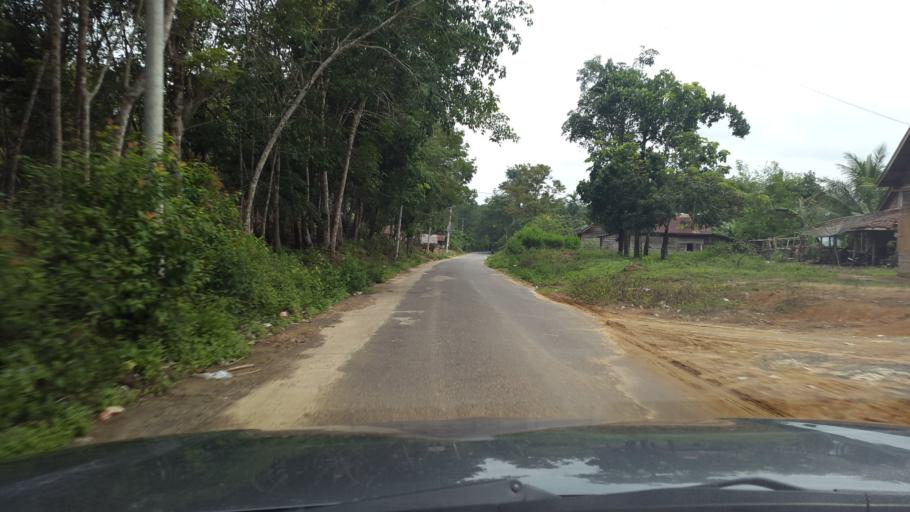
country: ID
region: South Sumatra
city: Gunungmenang
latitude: -3.1121
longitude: 103.8385
